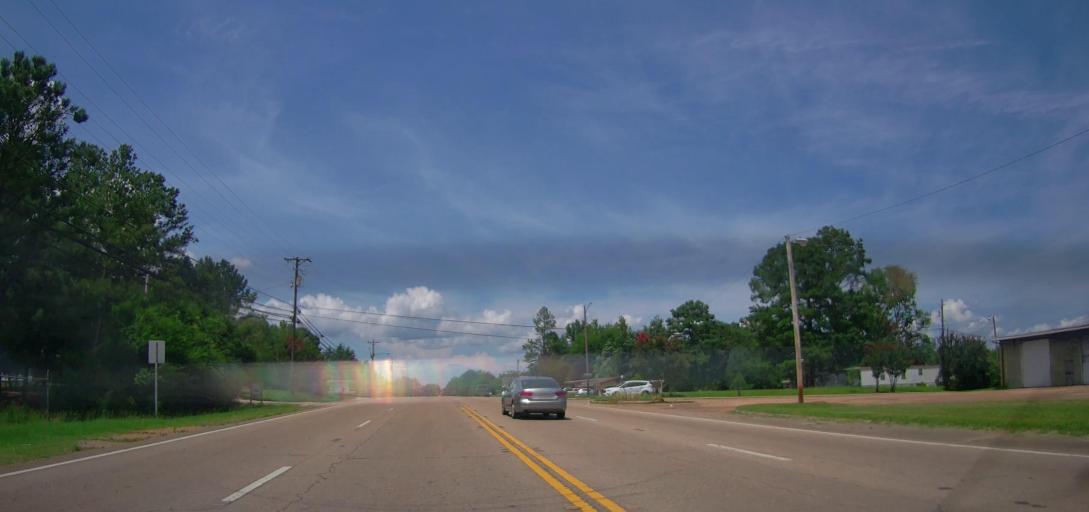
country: US
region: Mississippi
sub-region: Lee County
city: Verona
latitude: 34.1814
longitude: -88.7199
